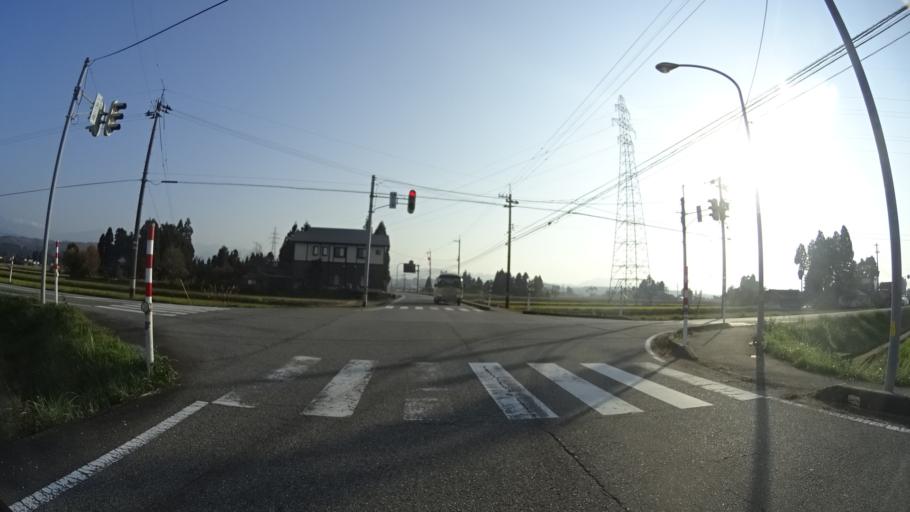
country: JP
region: Toyama
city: Kamiichi
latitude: 36.6255
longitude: 137.3157
